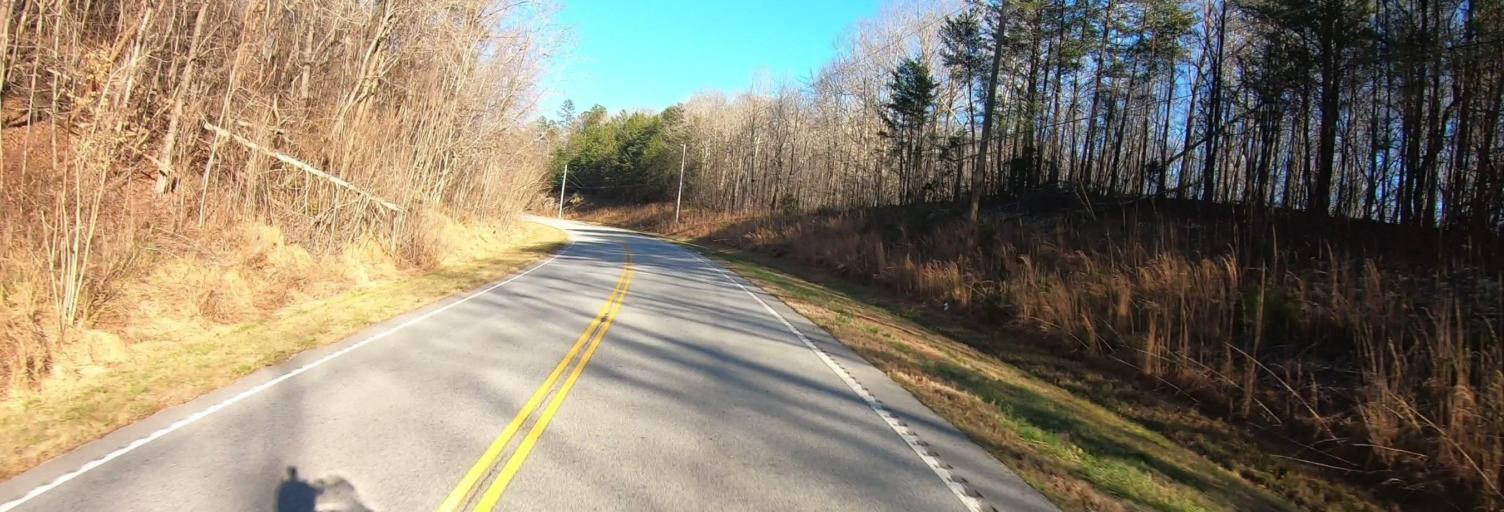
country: US
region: South Carolina
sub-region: Greenville County
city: Tigerville
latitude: 35.1056
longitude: -82.3573
